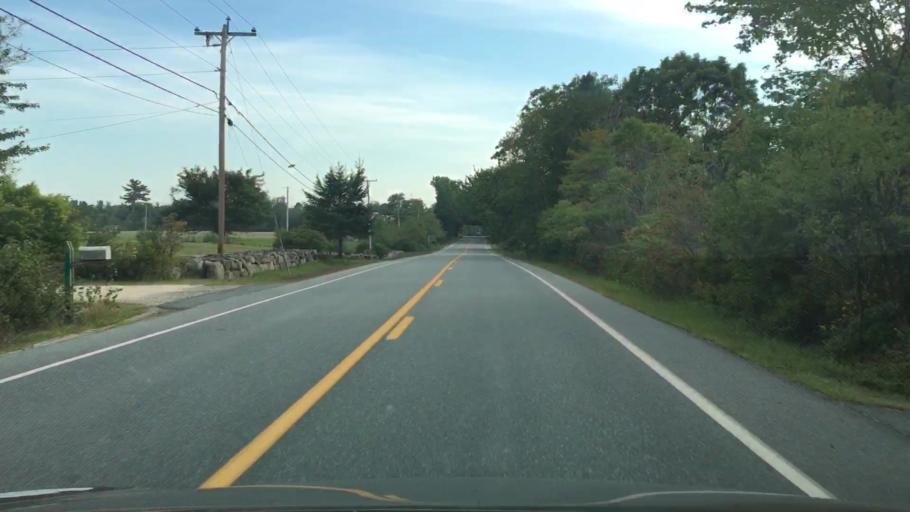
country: US
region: Maine
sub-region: Hancock County
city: Castine
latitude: 44.4408
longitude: -68.7891
